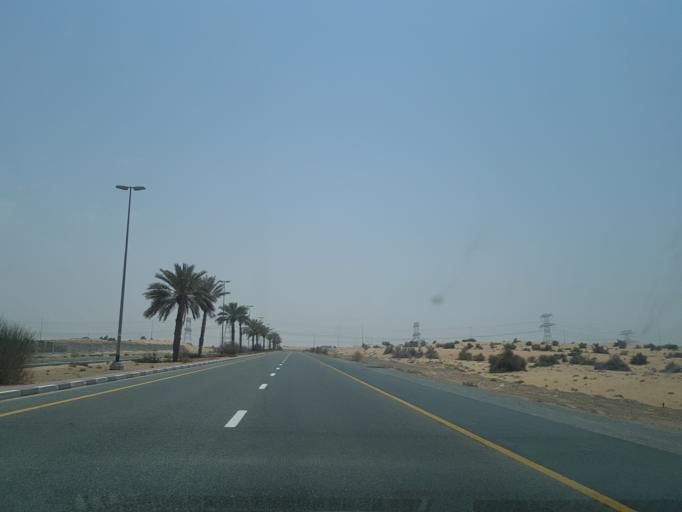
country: AE
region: Ash Shariqah
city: Sharjah
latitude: 25.1066
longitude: 55.4116
